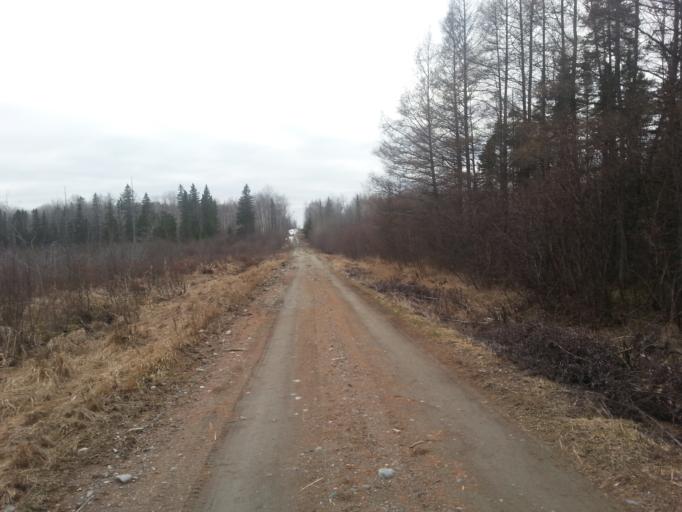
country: CA
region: Quebec
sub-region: Abitibi-Temiscamingue
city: Saint-Bruno-de-Guigues
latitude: 47.6331
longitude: -79.2506
